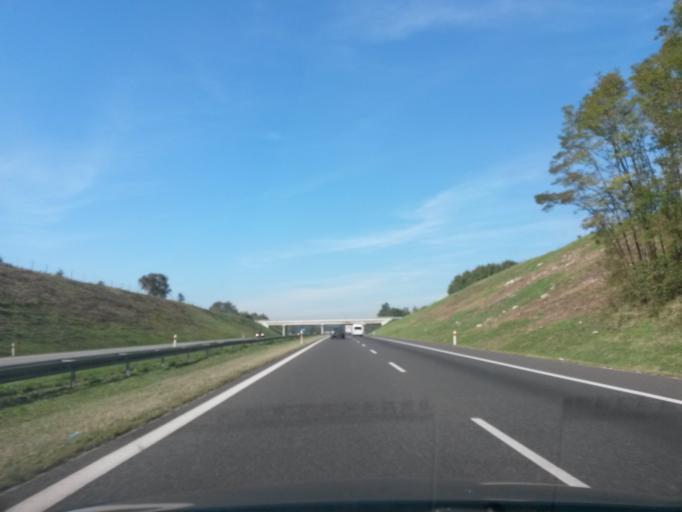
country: PL
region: Lesser Poland Voivodeship
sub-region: Powiat krakowski
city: Czulow
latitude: 50.0836
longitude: 19.7012
